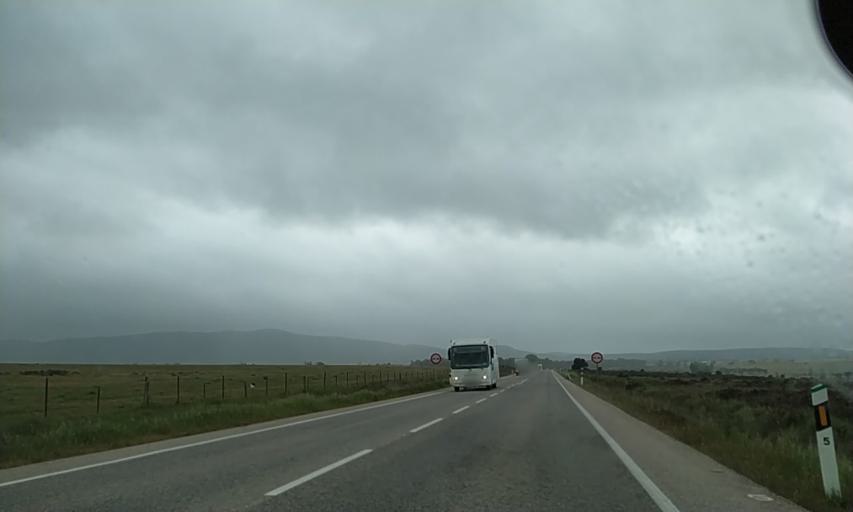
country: ES
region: Extremadura
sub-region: Provincia de Caceres
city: Malpartida de Caceres
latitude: 39.3382
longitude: -6.4799
